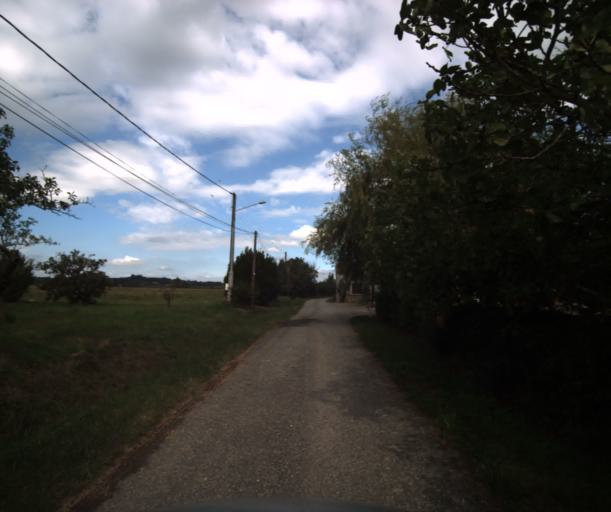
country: FR
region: Midi-Pyrenees
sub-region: Departement de la Haute-Garonne
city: Lacasse
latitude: 43.3991
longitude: 1.2361
